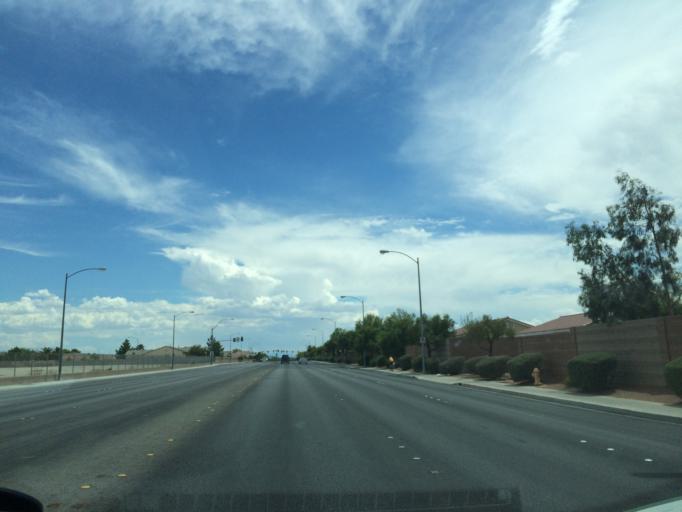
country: US
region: Nevada
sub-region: Clark County
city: North Las Vegas
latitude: 36.2578
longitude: -115.1801
